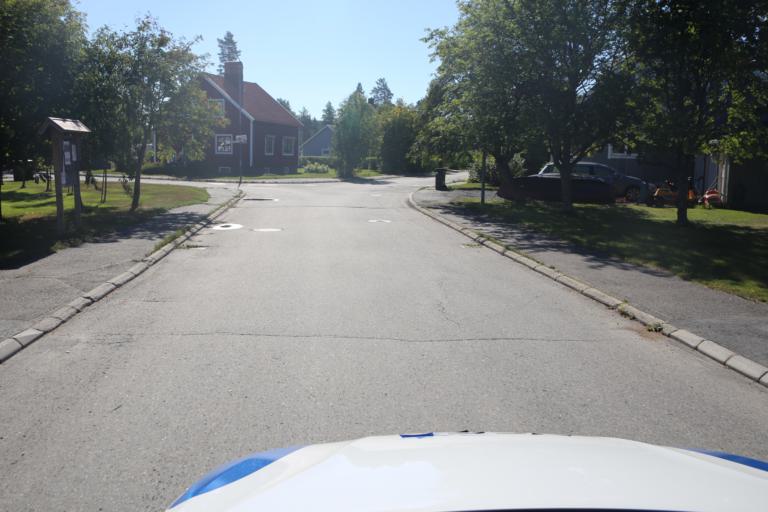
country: SE
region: Vaesterbotten
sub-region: Skelleftea Kommun
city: Viken
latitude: 64.7468
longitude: 20.7665
